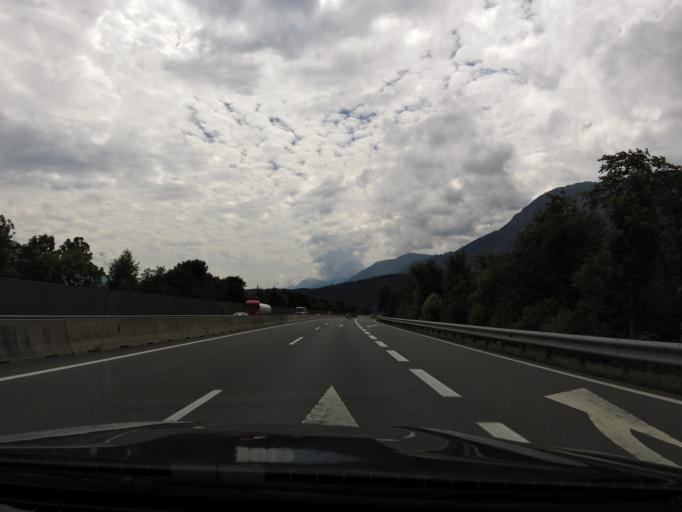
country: AT
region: Tyrol
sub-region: Politischer Bezirk Kufstein
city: Langkampfen
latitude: 47.5342
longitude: 12.0997
